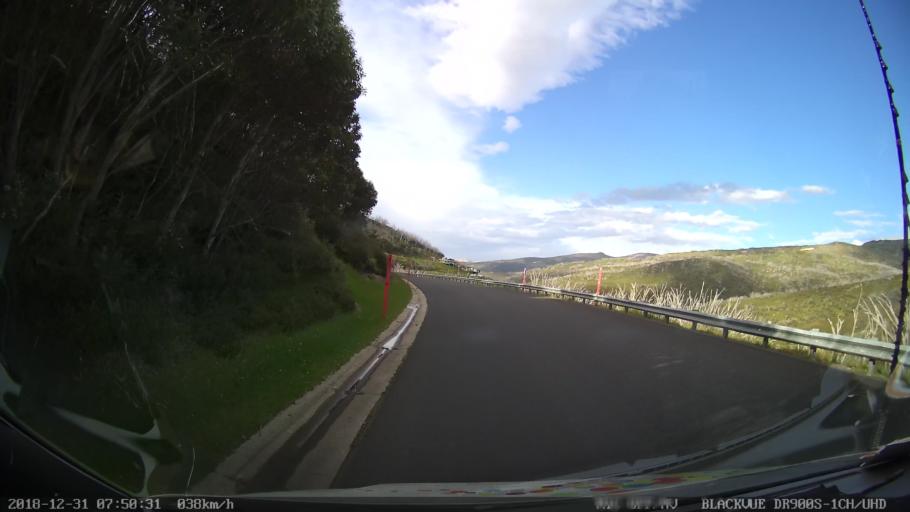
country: AU
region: New South Wales
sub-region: Snowy River
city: Jindabyne
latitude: -36.3742
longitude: 148.3799
